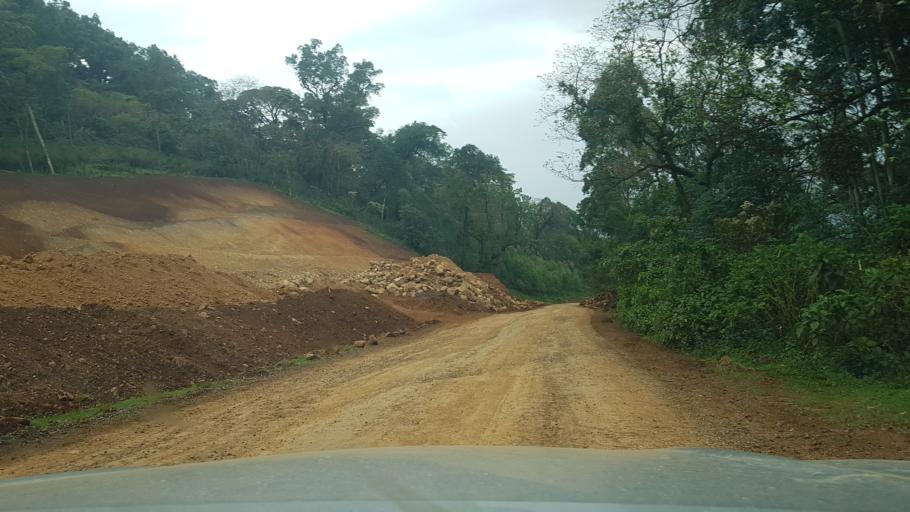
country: ET
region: Oromiya
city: Gore
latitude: 7.8264
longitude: 35.4624
